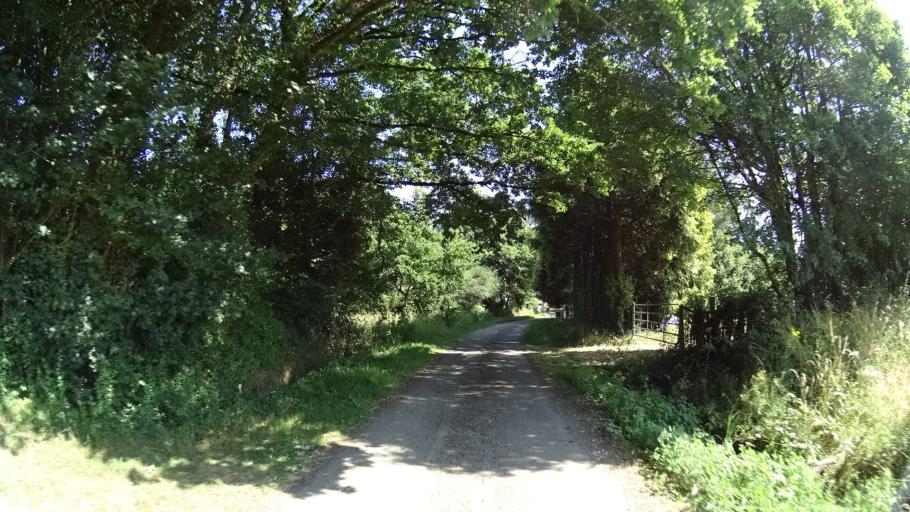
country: FR
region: Brittany
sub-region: Departement d'Ille-et-Vilaine
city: Orgeres
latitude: 47.9794
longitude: -1.6464
